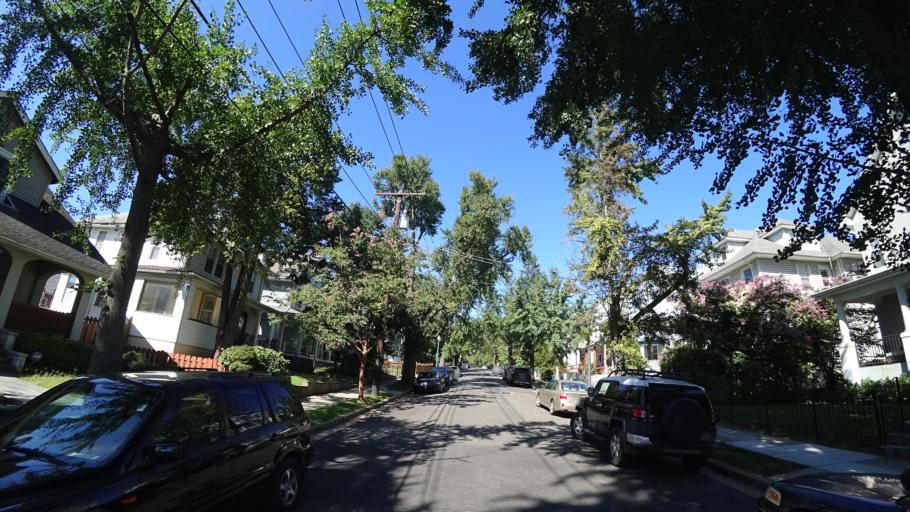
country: US
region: Maryland
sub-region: Montgomery County
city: Takoma Park
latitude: 38.9490
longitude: -77.0309
